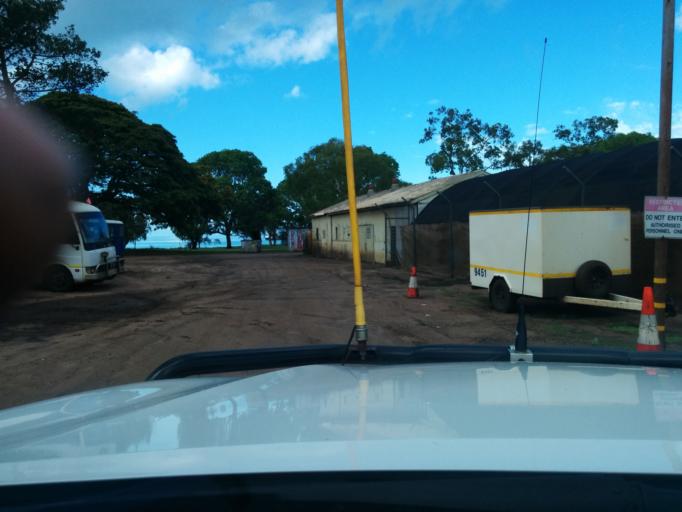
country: AU
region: Northern Territory
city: Alyangula
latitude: -13.8486
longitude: 136.4162
